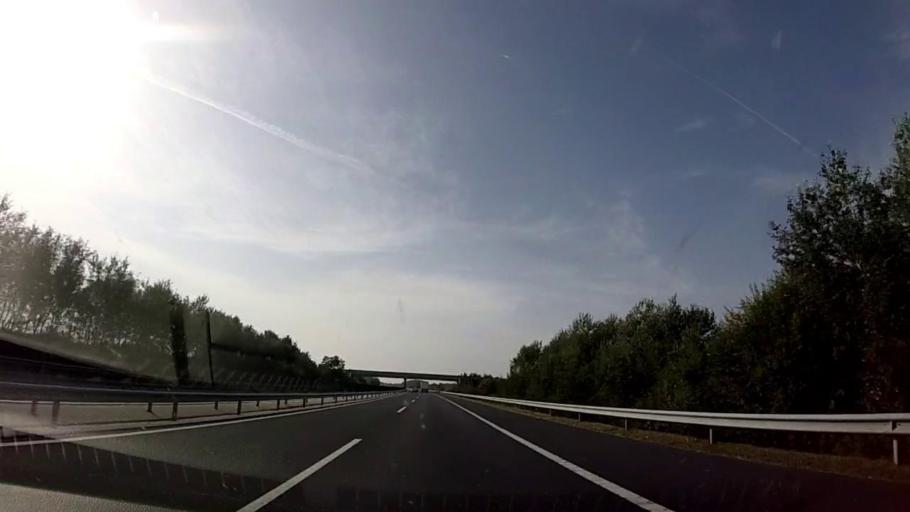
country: HU
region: Zala
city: Zalakomar
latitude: 46.5530
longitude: 17.2185
